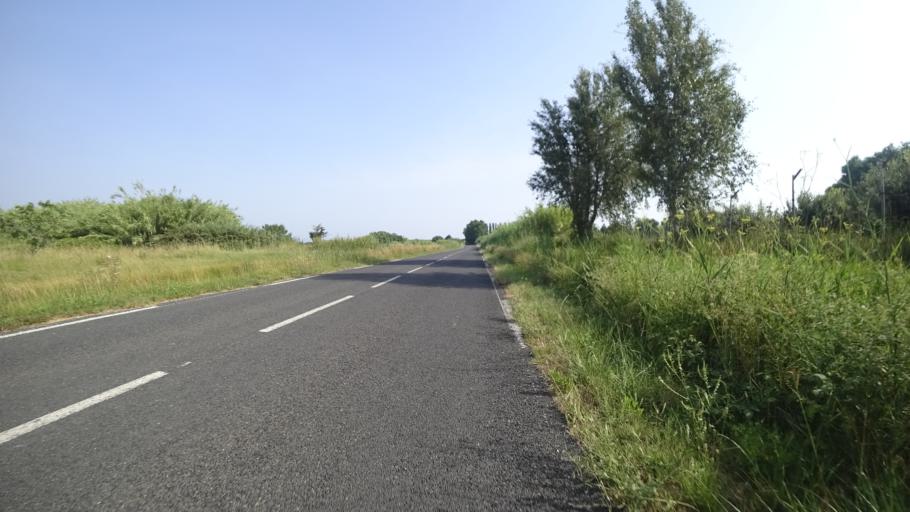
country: FR
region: Languedoc-Roussillon
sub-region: Departement des Pyrenees-Orientales
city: Villelongue-de-la-Salanque
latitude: 42.7376
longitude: 2.9894
